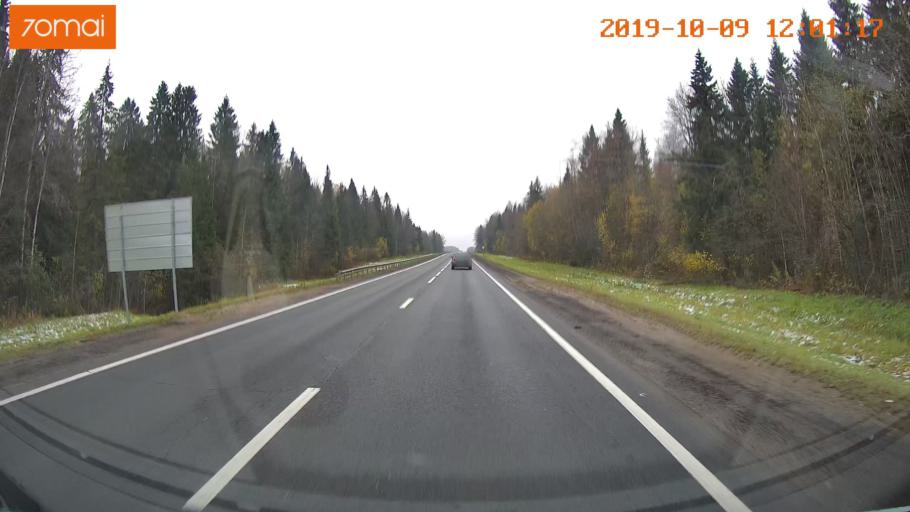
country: RU
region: Vologda
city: Gryazovets
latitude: 58.6898
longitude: 40.3027
